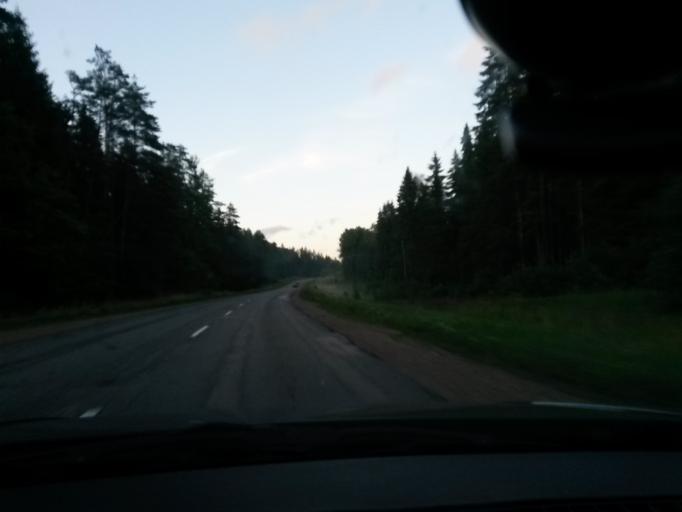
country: LV
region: Madonas Rajons
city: Madona
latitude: 56.8228
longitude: 26.1559
